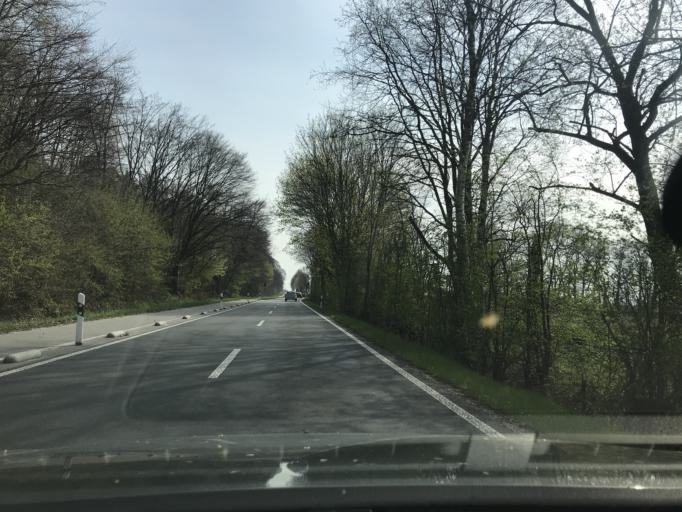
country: DE
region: North Rhine-Westphalia
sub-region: Regierungsbezirk Dusseldorf
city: Kleve
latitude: 51.7369
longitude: 6.1674
